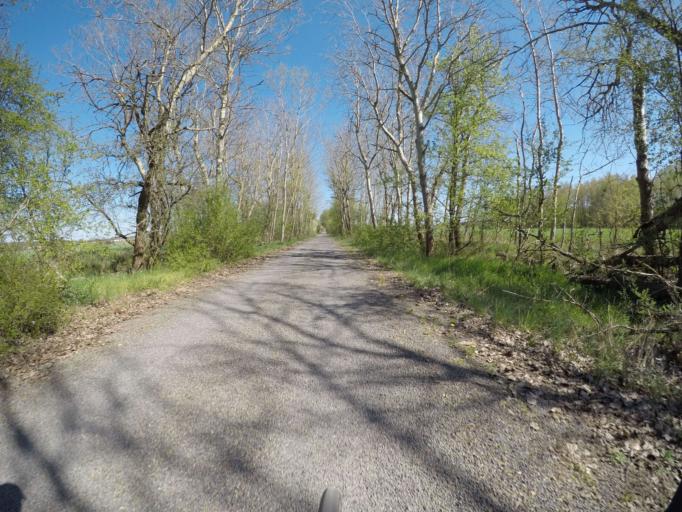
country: DE
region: Brandenburg
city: Werftpfuhl
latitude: 52.6390
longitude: 13.7771
